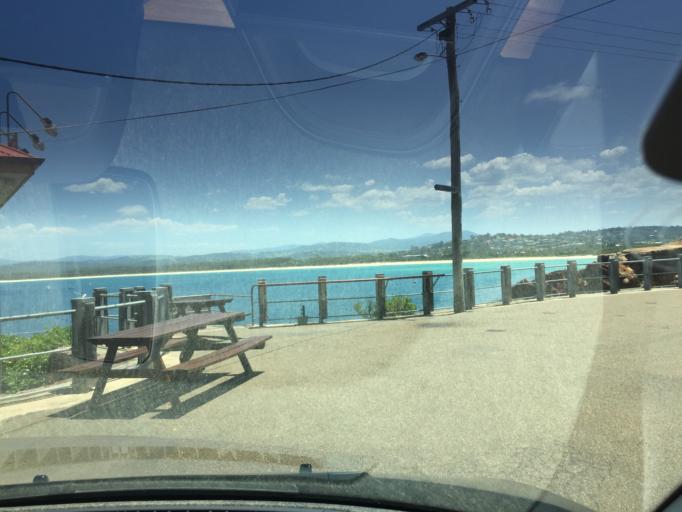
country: AU
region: New South Wales
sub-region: Bega Valley
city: Merimbula
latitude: -36.8986
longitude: 149.9276
